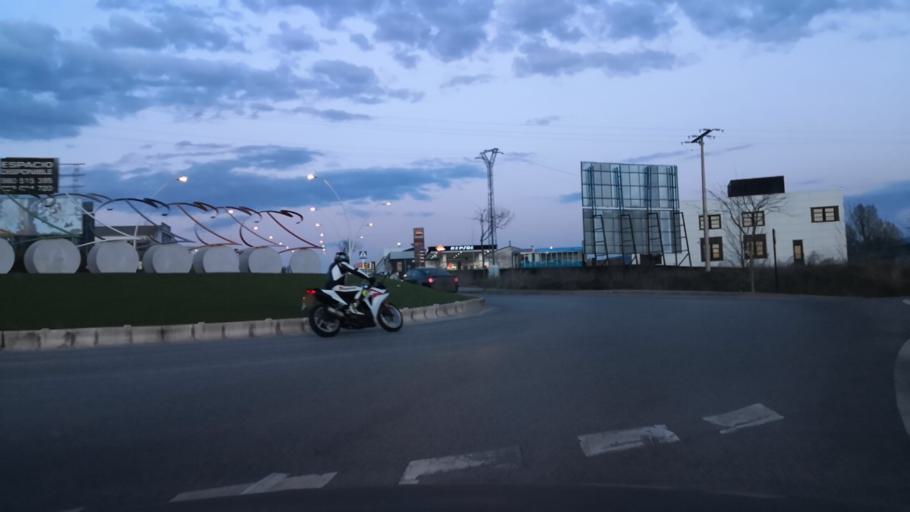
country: ES
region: Castille and Leon
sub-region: Provincia de Leon
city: Ponferrada
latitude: 42.5508
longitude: -6.5783
